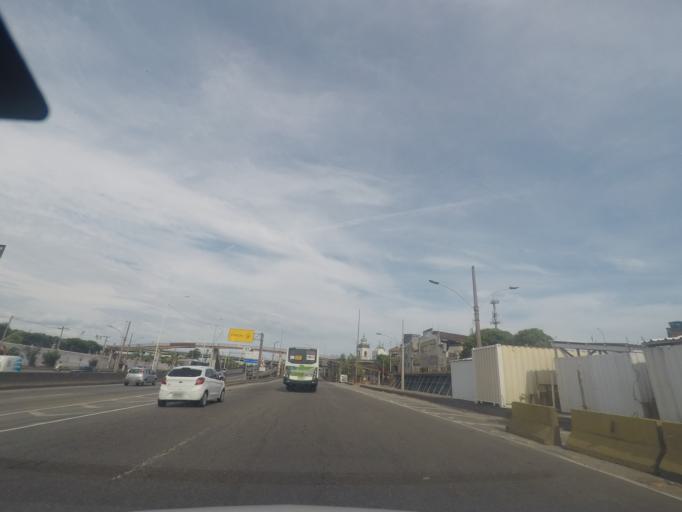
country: BR
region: Rio de Janeiro
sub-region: Rio De Janeiro
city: Rio de Janeiro
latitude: -22.8891
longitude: -43.2216
